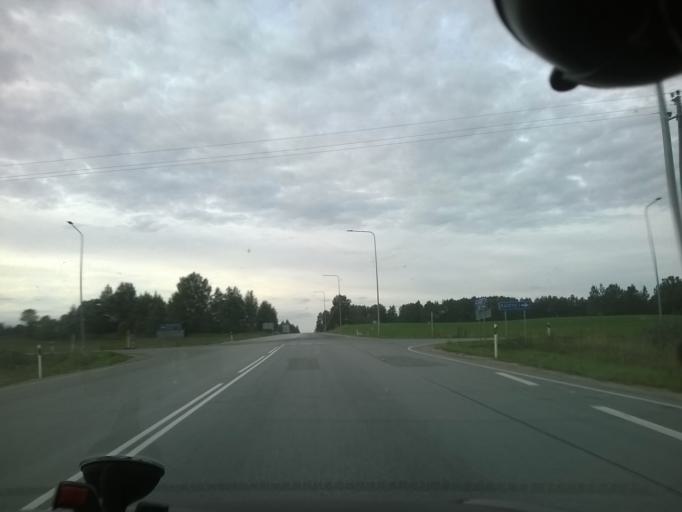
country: EE
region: Vorumaa
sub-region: Voru linn
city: Voru
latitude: 57.8916
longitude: 26.8491
